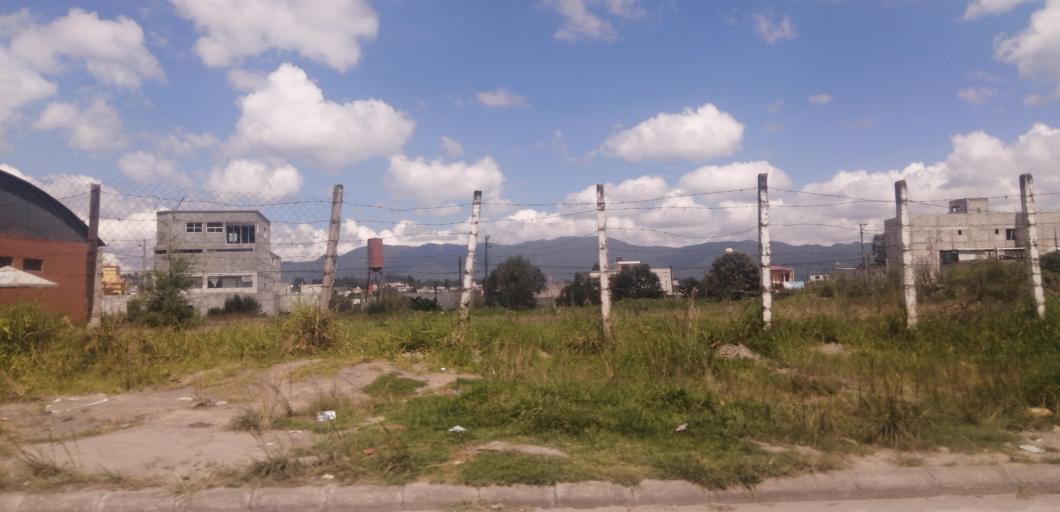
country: GT
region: Quetzaltenango
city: Quetzaltenango
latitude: 14.8279
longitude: -91.5299
